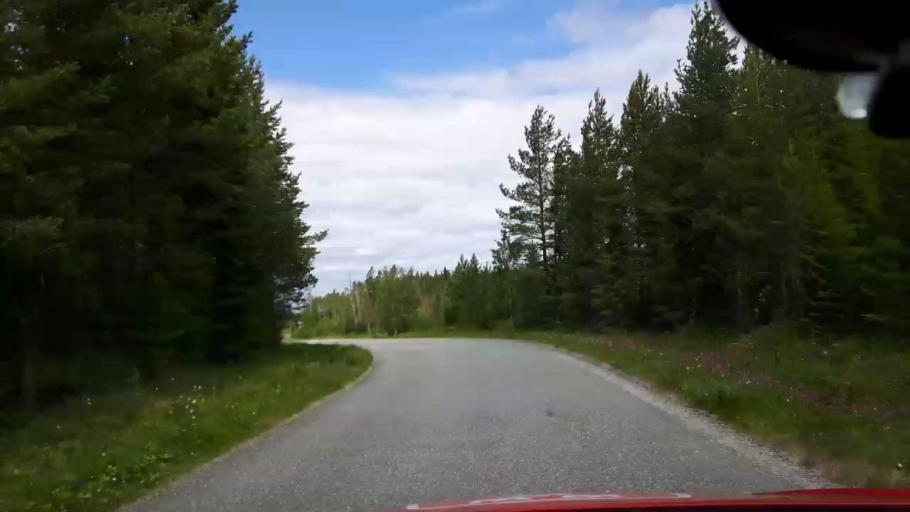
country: SE
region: Jaemtland
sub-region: Braecke Kommun
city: Braecke
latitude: 62.8350
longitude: 15.3074
